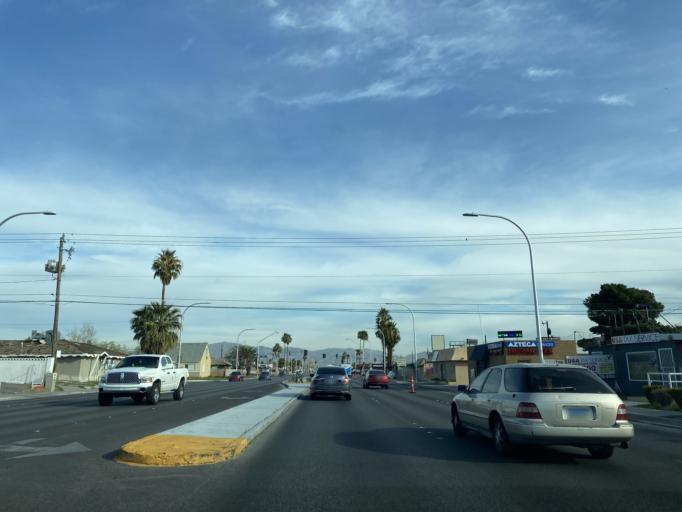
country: US
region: Nevada
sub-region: Clark County
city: Winchester
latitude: 36.1503
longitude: -115.1188
